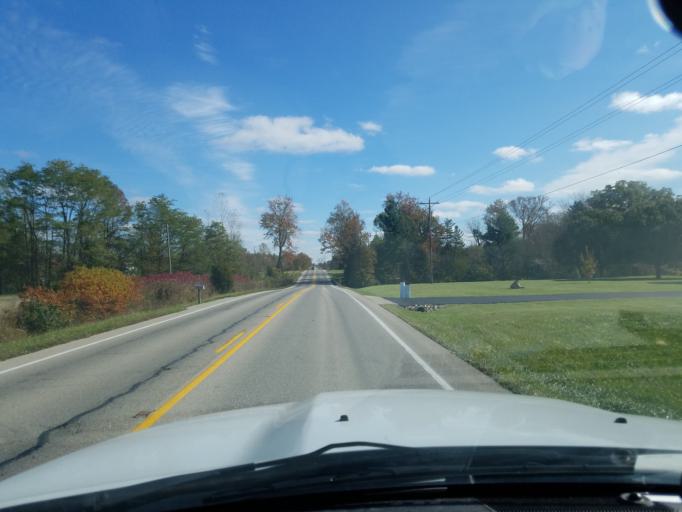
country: US
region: Indiana
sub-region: Ripley County
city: Osgood
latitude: 39.0751
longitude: -85.3365
